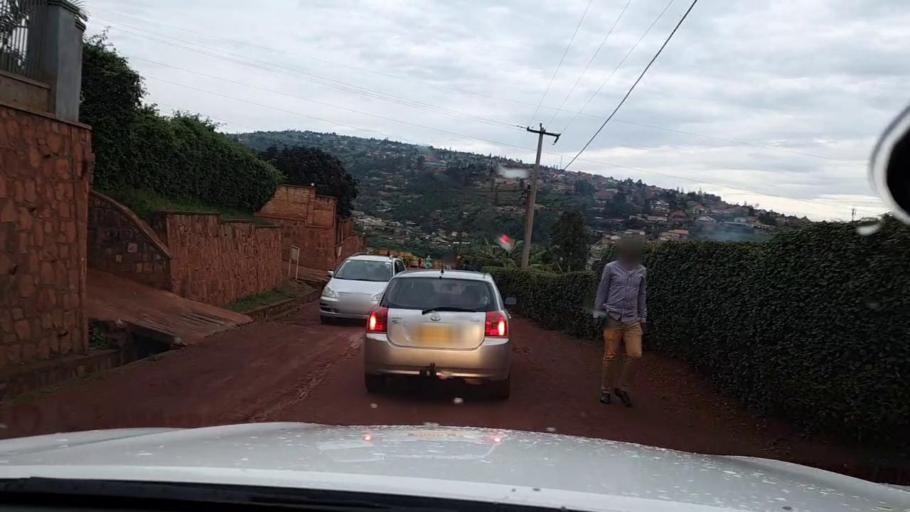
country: RW
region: Kigali
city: Kigali
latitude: -1.9043
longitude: 30.0490
